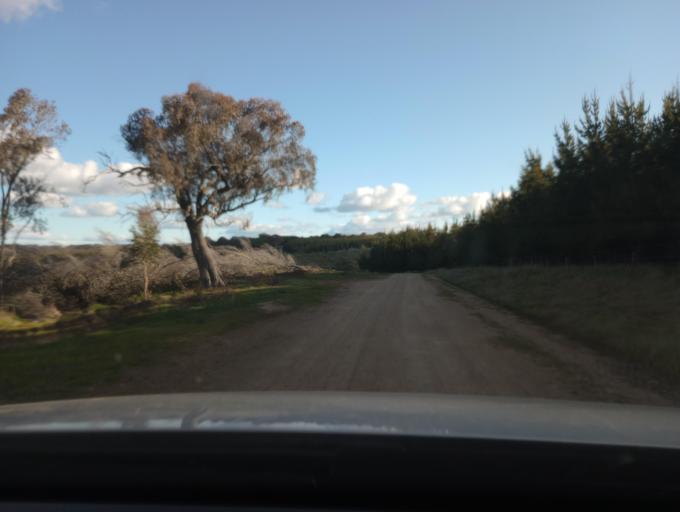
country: AU
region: New South Wales
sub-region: Blayney
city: Millthorpe
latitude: -33.4005
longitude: 149.3159
